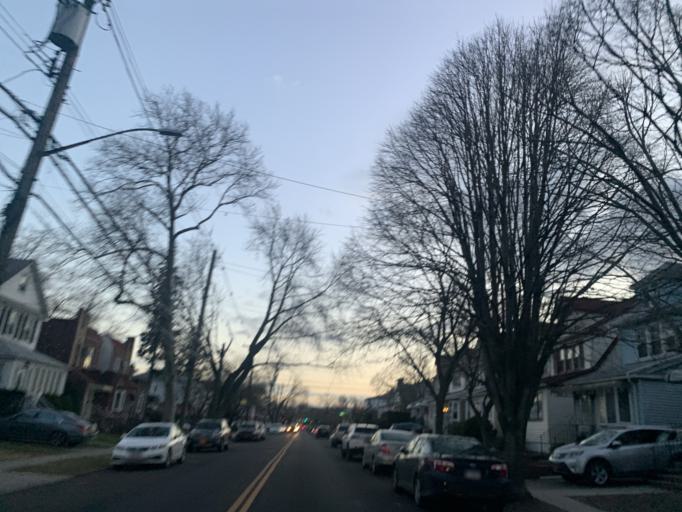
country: US
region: New York
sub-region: Nassau County
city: East Atlantic Beach
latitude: 40.7798
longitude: -73.8172
